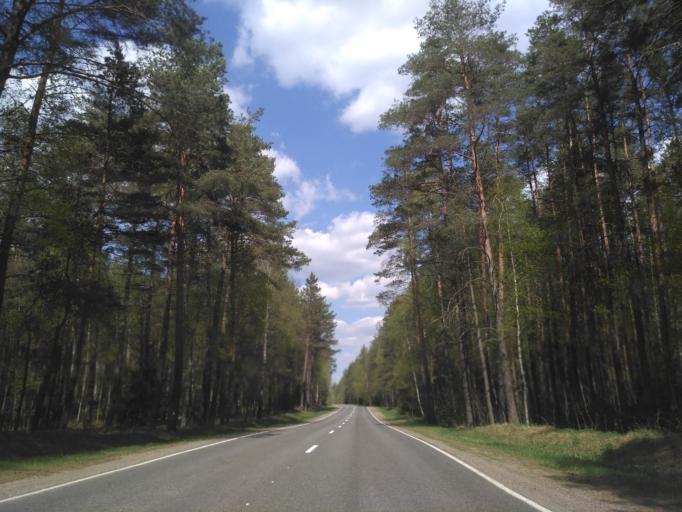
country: BY
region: Minsk
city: Myadzyel
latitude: 54.7467
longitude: 26.9486
